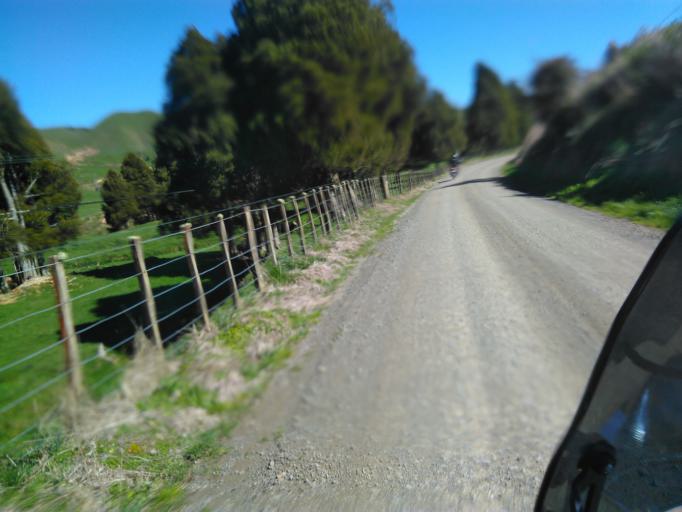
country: NZ
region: Bay of Plenty
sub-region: Opotiki District
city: Opotiki
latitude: -38.2986
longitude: 177.5559
